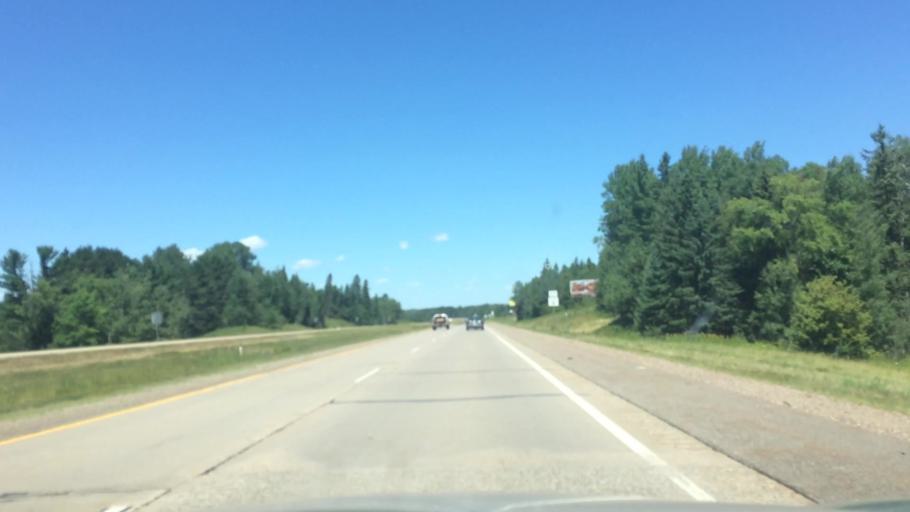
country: US
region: Wisconsin
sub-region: Lincoln County
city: Tomahawk
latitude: 45.3627
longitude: -89.6668
